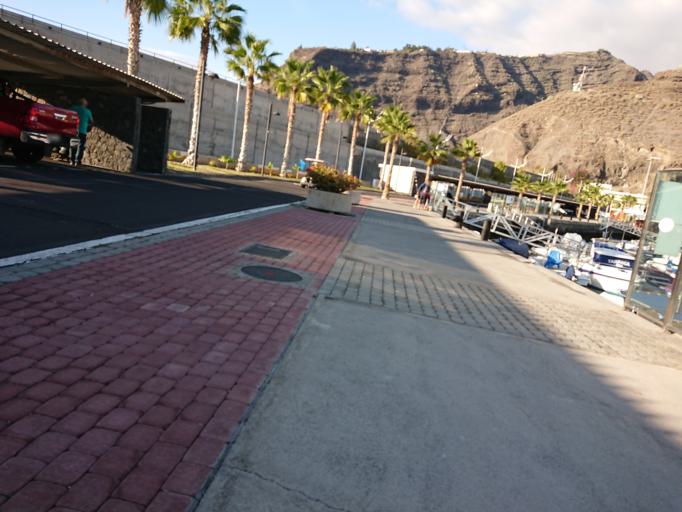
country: ES
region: Canary Islands
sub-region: Provincia de Santa Cruz de Tenerife
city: Tazacorte
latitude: 28.6452
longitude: -17.9444
